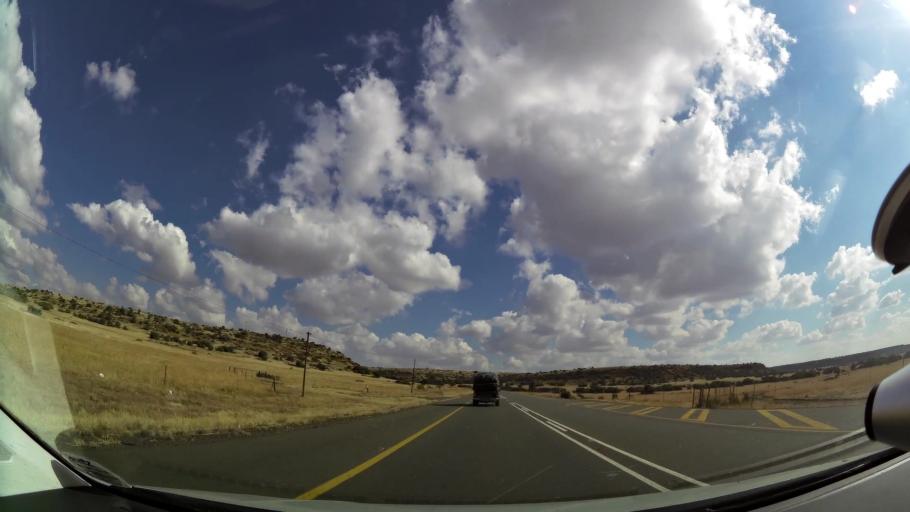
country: ZA
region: Orange Free State
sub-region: Mangaung Metropolitan Municipality
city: Bloemfontein
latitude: -29.1482
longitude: 26.0664
